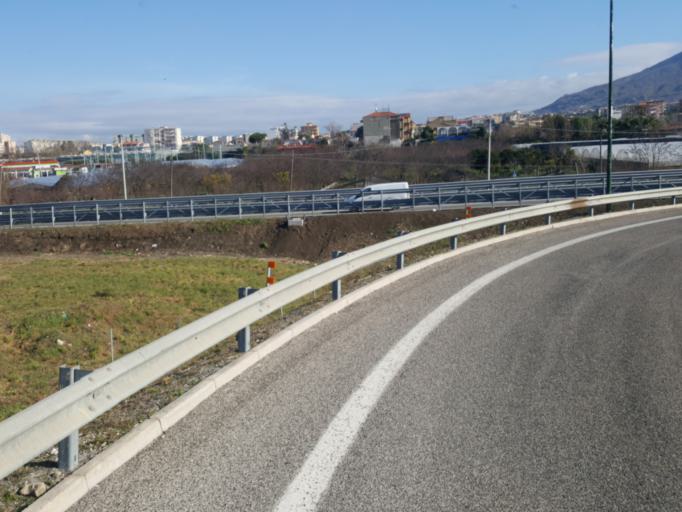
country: IT
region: Campania
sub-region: Provincia di Napoli
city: San Giorgio a Cremano
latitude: 40.8407
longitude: 14.3325
